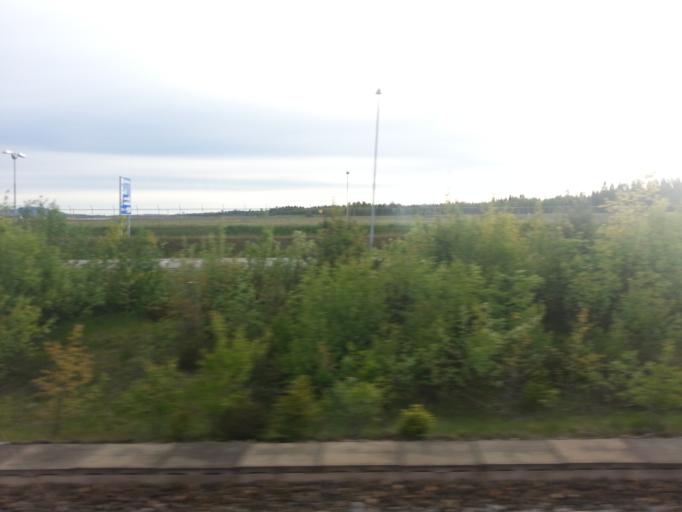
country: NO
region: Akershus
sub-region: Ullensaker
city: Jessheim
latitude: 60.1686
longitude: 11.1078
